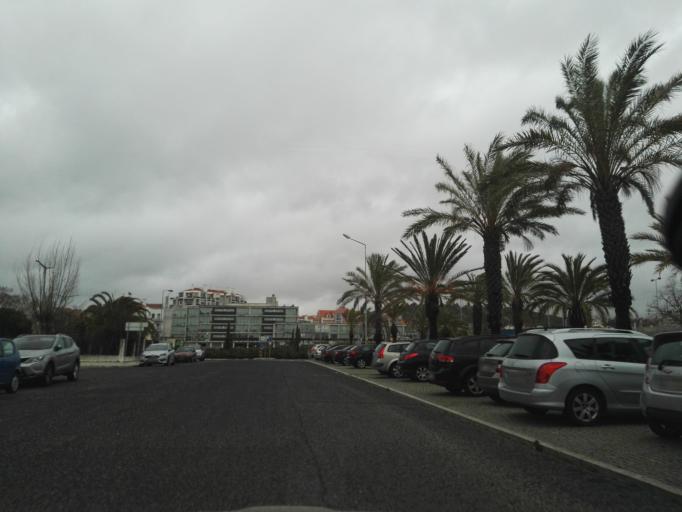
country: PT
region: Lisbon
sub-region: Oeiras
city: Alges
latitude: 38.6970
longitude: -9.2298
